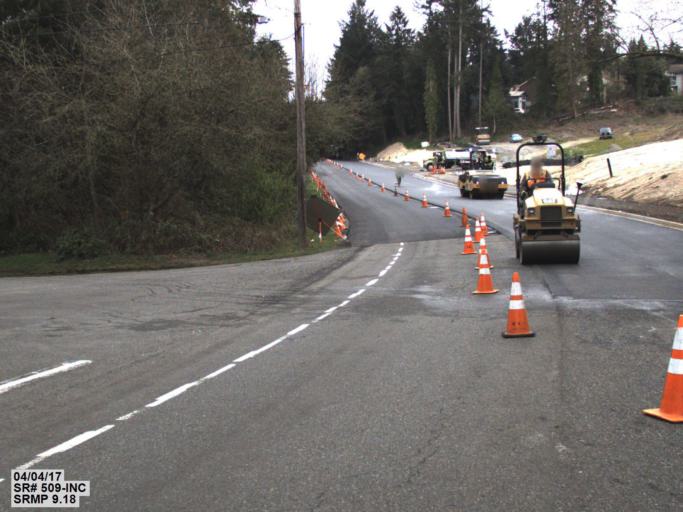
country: US
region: Washington
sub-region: Pierce County
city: Fife Heights
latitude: 47.3216
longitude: -122.3903
